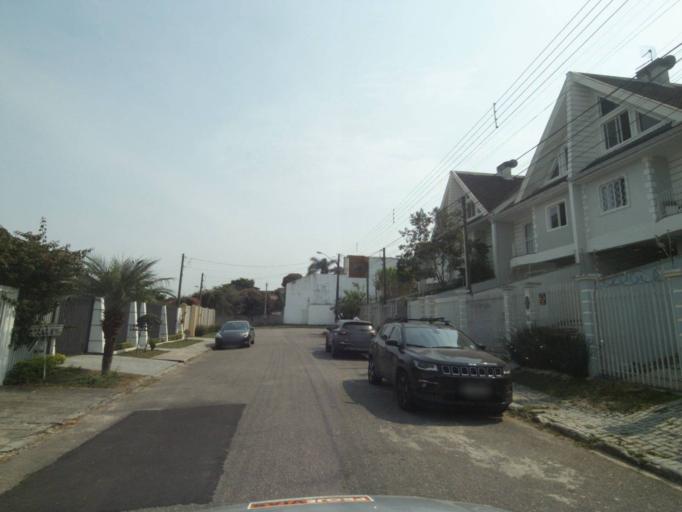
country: BR
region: Parana
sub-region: Pinhais
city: Pinhais
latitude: -25.4779
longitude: -49.2229
